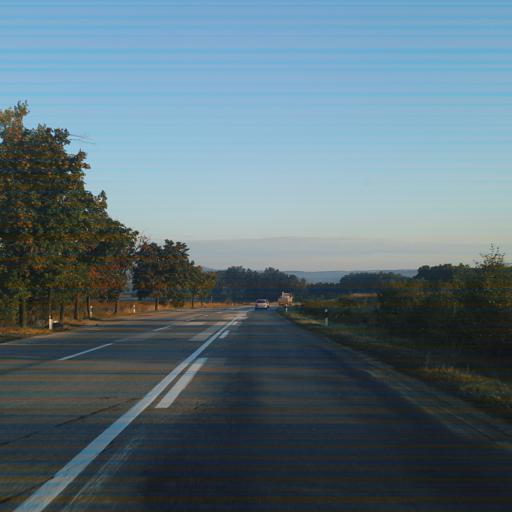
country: RS
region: Central Serbia
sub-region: Zajecarski Okrug
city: Zajecar
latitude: 44.0701
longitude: 22.3342
